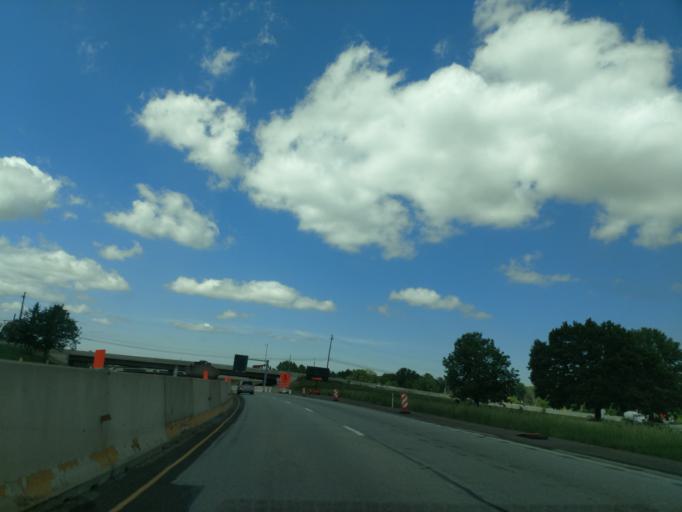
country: US
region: Pennsylvania
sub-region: Montgomery County
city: King of Prussia
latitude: 40.0995
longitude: -75.4181
